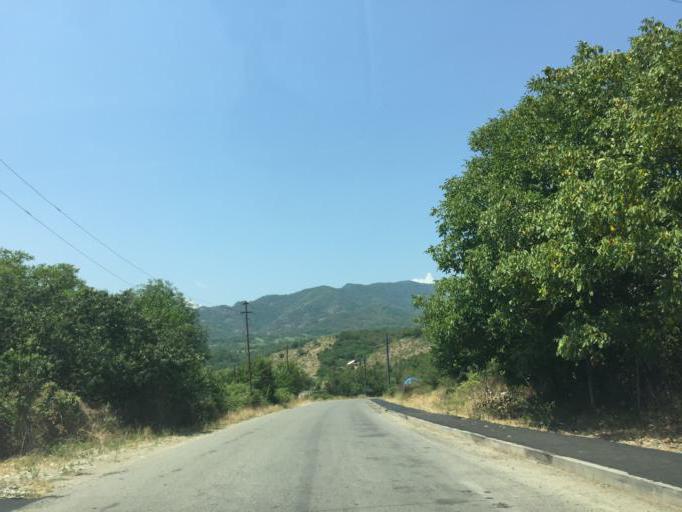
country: AZ
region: Tartar Rayon
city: Martakert
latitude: 40.1304
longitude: 46.4554
